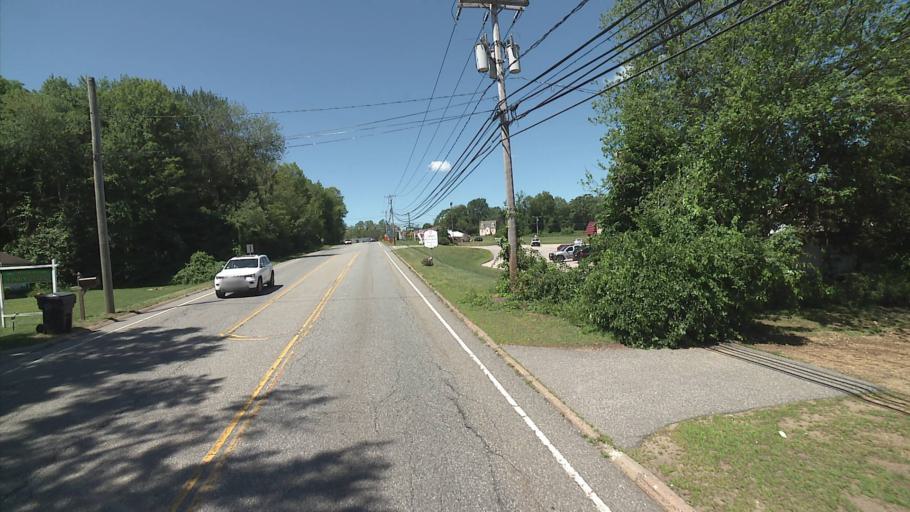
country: US
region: Connecticut
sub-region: Middlesex County
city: Moodus
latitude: 41.5461
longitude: -72.4107
